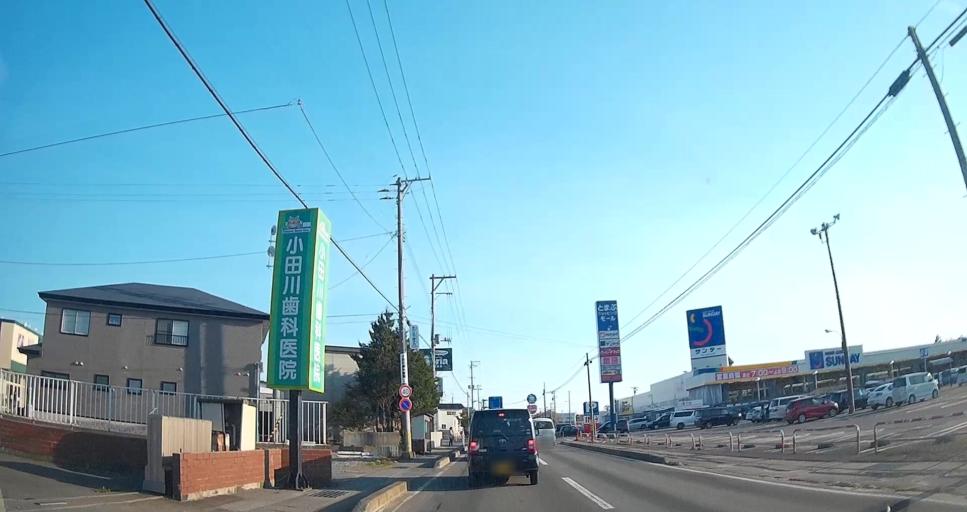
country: JP
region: Aomori
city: Mutsu
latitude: 41.2853
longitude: 141.2113
